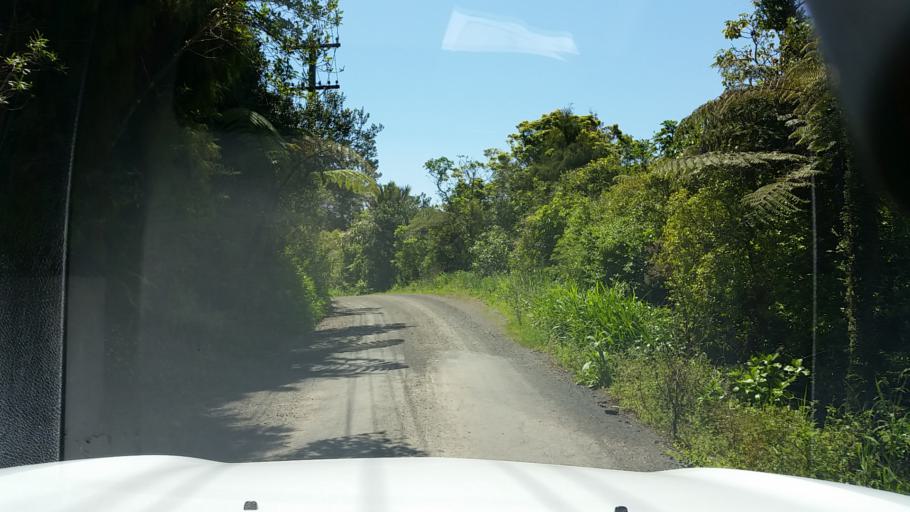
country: NZ
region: Auckland
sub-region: Auckland
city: Titirangi
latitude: -36.9308
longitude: 174.5810
